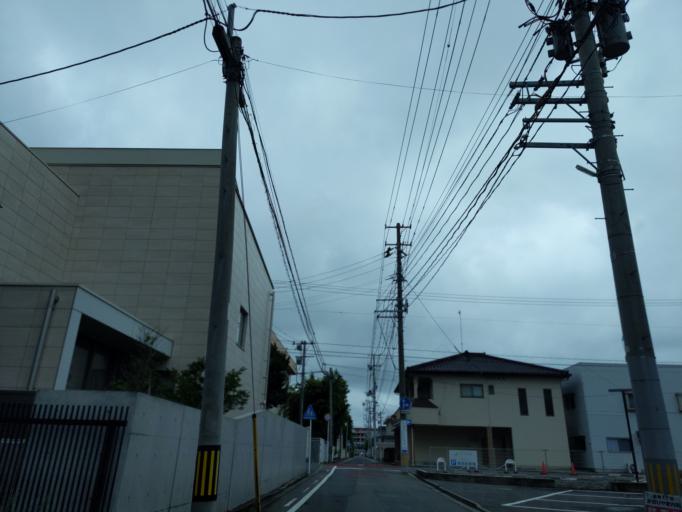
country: JP
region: Fukushima
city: Koriyama
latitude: 37.4019
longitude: 140.3707
